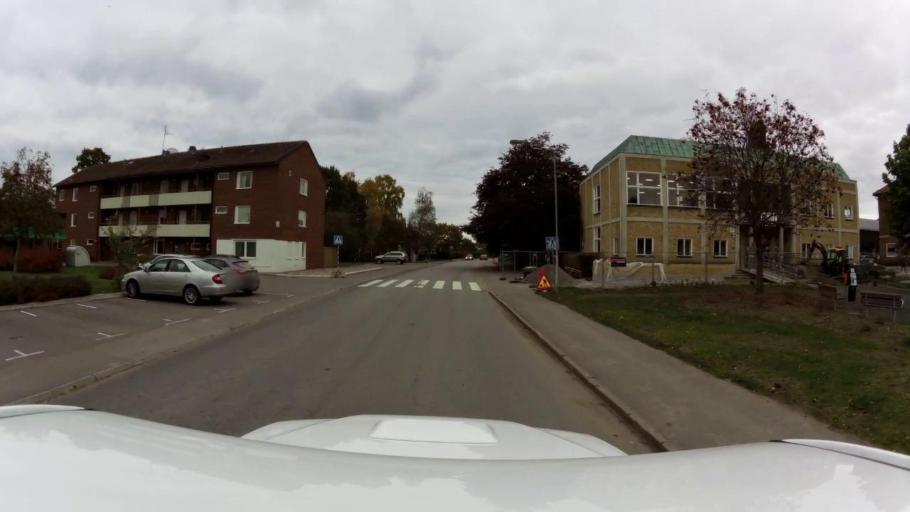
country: SE
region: OEstergoetland
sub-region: Linkopings Kommun
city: Ljungsbro
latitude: 58.5092
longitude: 15.5031
